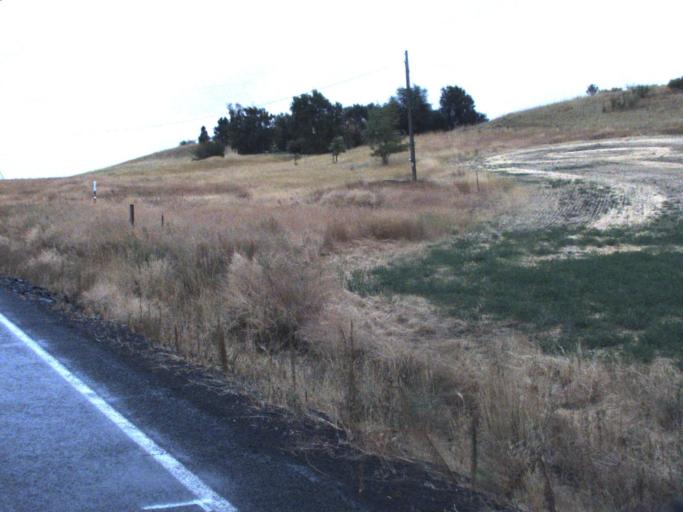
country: US
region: Washington
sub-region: Lincoln County
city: Davenport
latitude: 47.3580
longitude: -118.0405
